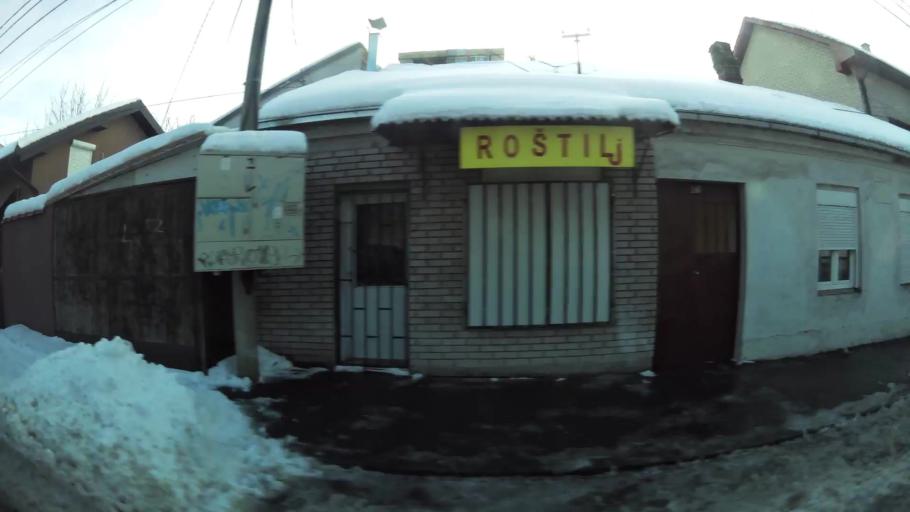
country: RS
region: Central Serbia
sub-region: Belgrade
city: Palilula
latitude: 44.8033
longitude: 20.4956
